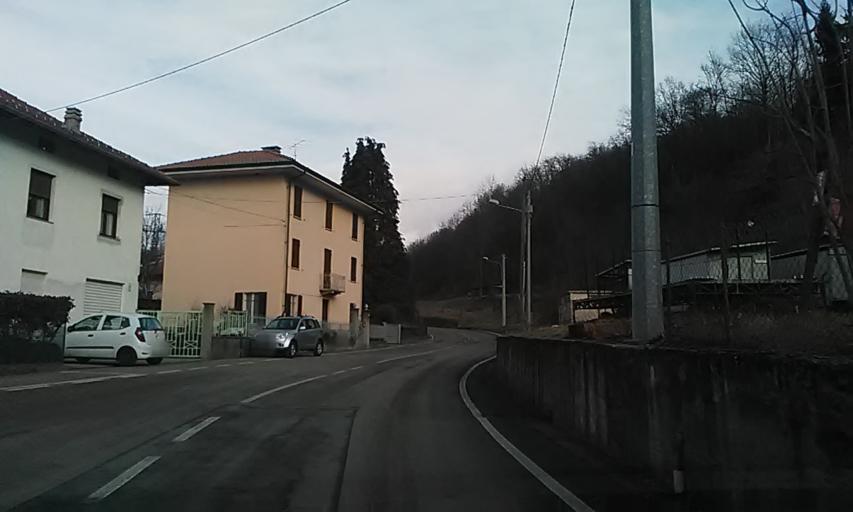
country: IT
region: Piedmont
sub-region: Provincia di Vercelli
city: Borgosesia
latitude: 45.7239
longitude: 8.2836
